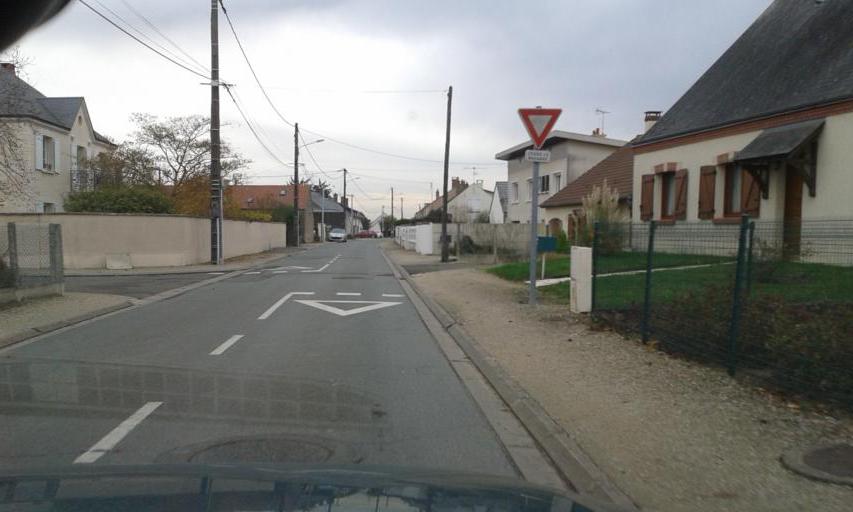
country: FR
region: Centre
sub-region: Departement du Loiret
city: Gidy
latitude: 47.9833
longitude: 1.8364
